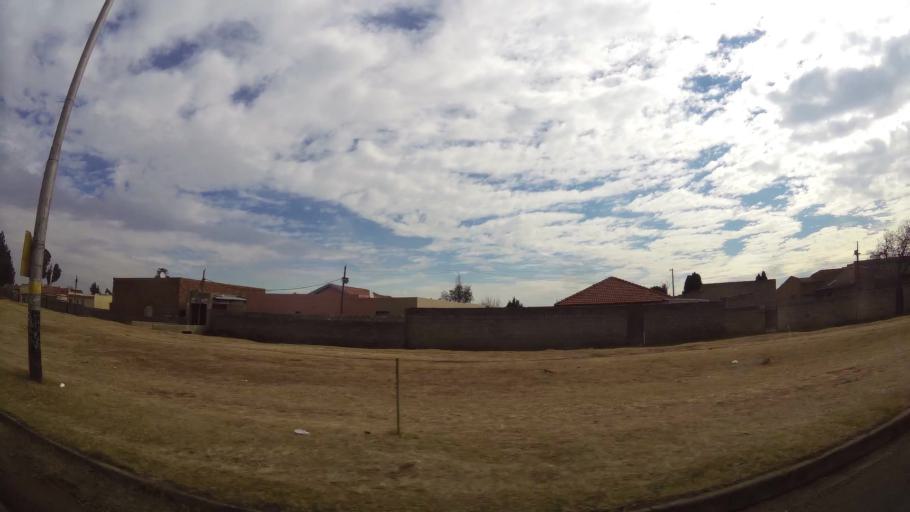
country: ZA
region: Gauteng
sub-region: Ekurhuleni Metropolitan Municipality
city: Germiston
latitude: -26.3275
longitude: 28.1810
